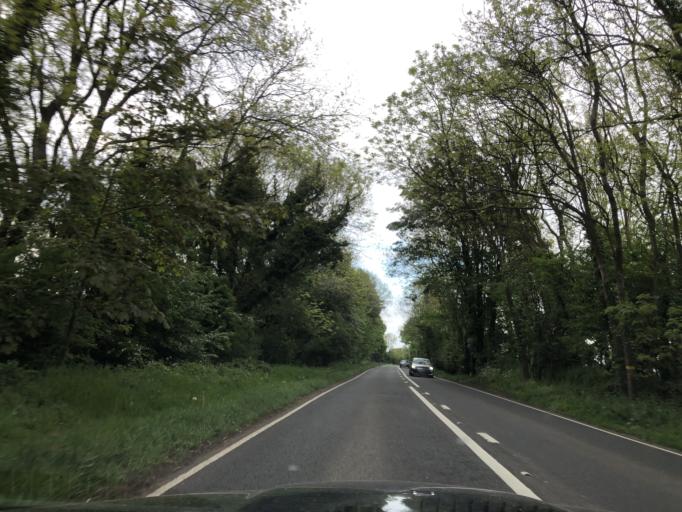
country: GB
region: England
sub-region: Gloucestershire
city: Stow on the Wold
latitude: 51.9376
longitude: -1.7228
